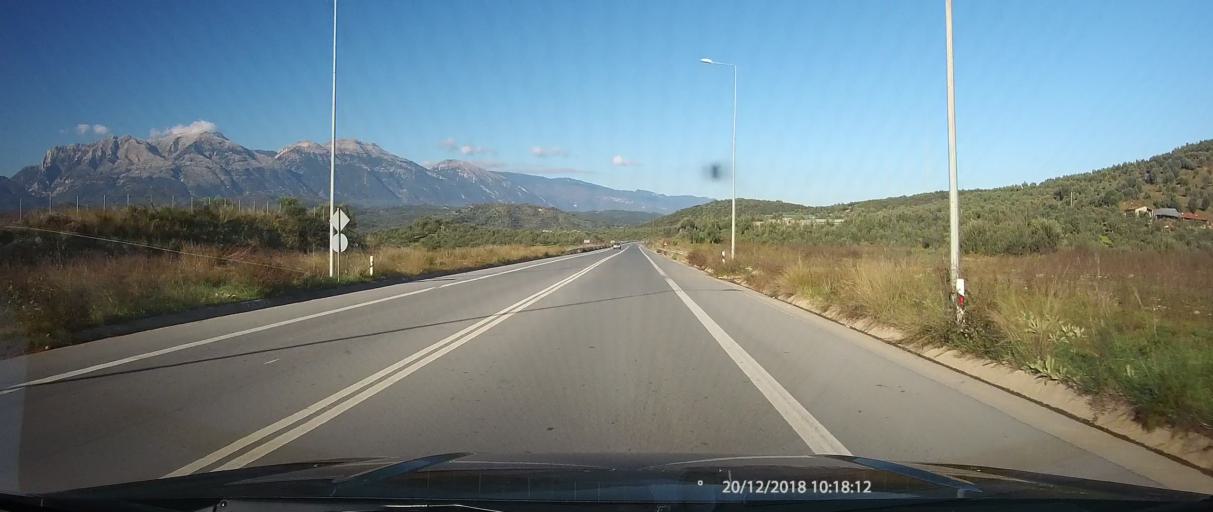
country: GR
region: Peloponnese
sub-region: Nomos Lakonias
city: Sparti
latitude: 37.1145
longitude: 22.4281
